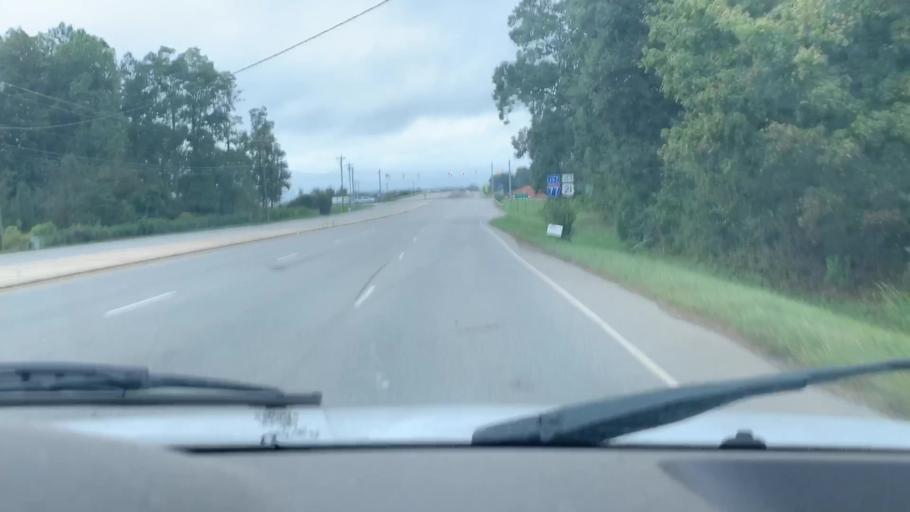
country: US
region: North Carolina
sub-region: Gaston County
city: Davidson
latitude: 35.5329
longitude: -80.8584
